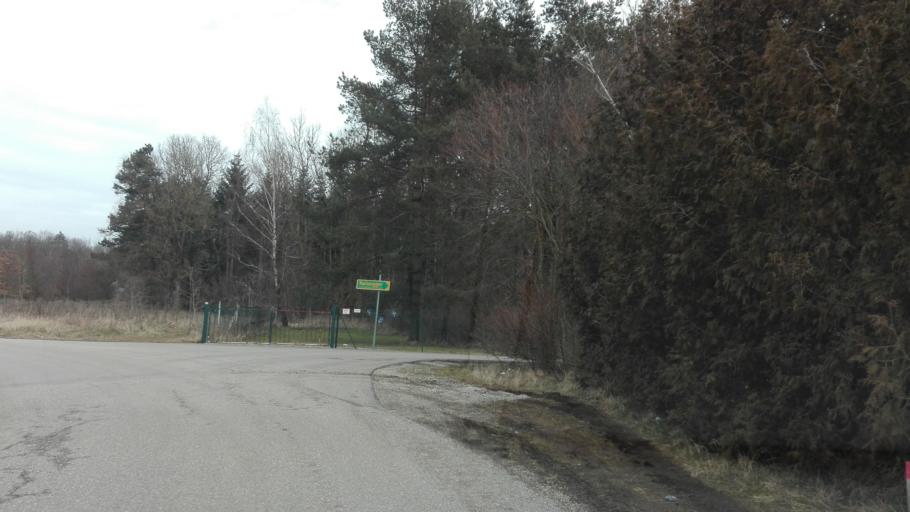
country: AT
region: Upper Austria
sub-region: Politischer Bezirk Linz-Land
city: Traun
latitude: 48.2330
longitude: 14.2175
